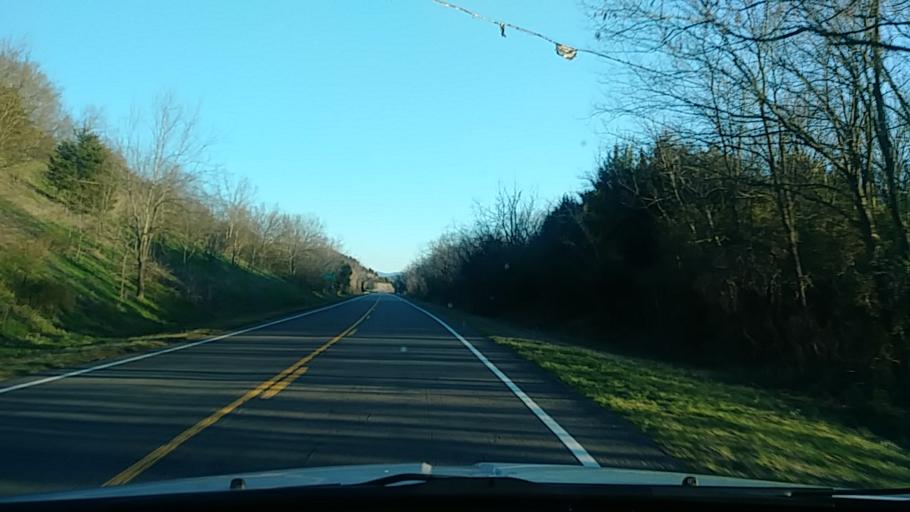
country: US
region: Tennessee
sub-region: Hamblen County
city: Morristown
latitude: 36.1821
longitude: -83.1659
